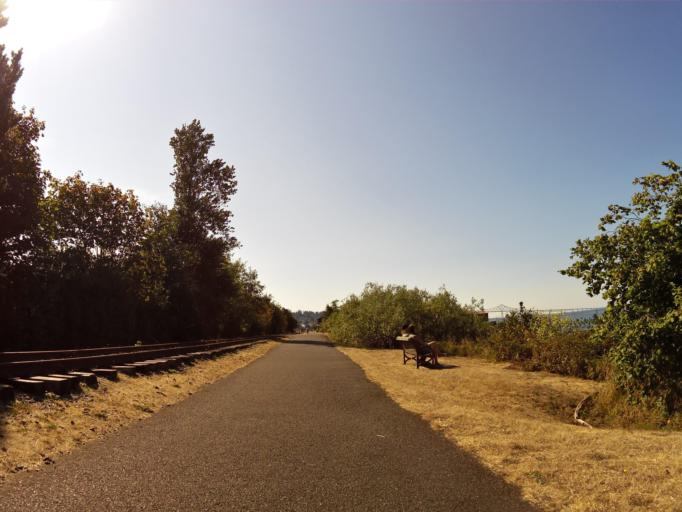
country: US
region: Oregon
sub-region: Clatsop County
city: Astoria
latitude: 46.1936
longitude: -123.8060
